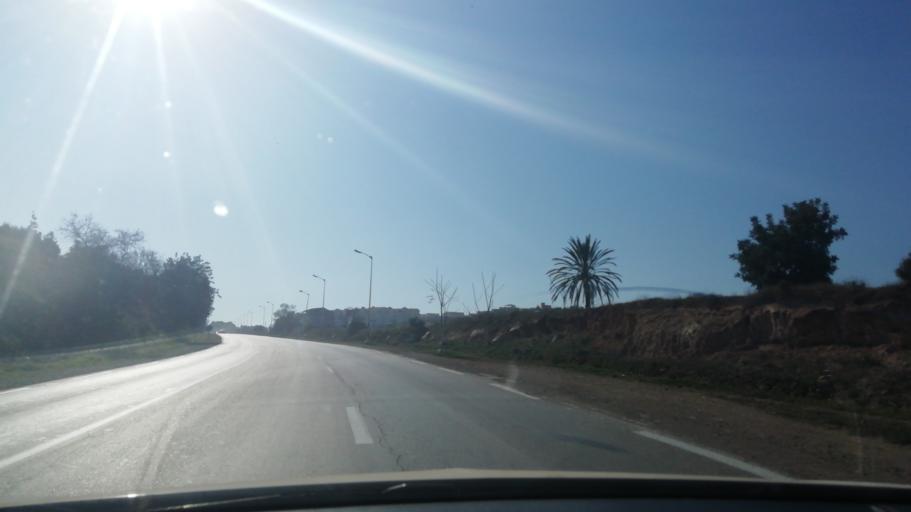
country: DZ
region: Tlemcen
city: Nedroma
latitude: 35.1021
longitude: -1.8340
